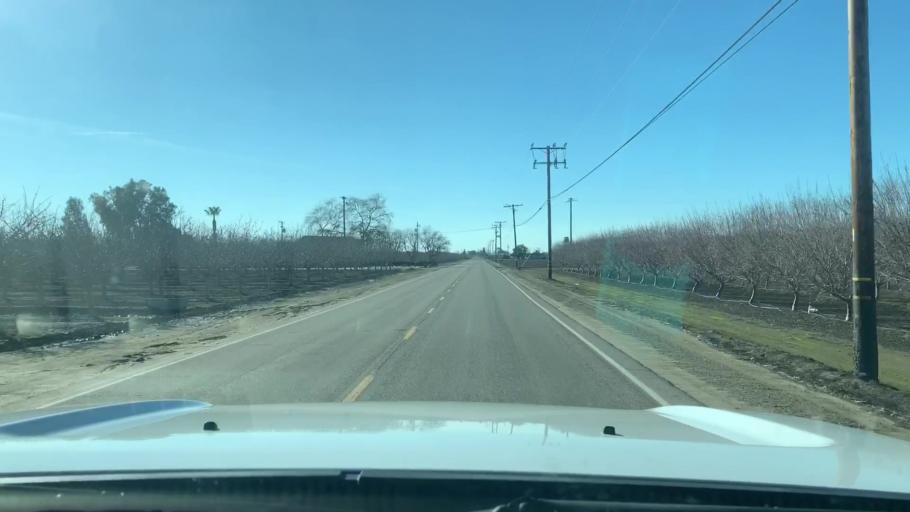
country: US
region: California
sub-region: Tulare County
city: Tulare
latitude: 36.1813
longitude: -119.4471
